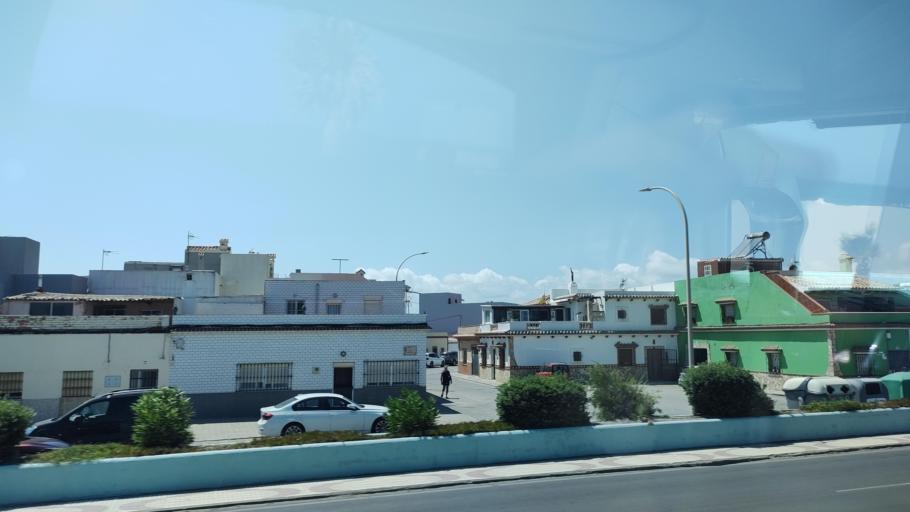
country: ES
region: Andalusia
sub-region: Provincia de Cadiz
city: La Linea de la Concepcion
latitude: 36.1707
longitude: -5.3375
